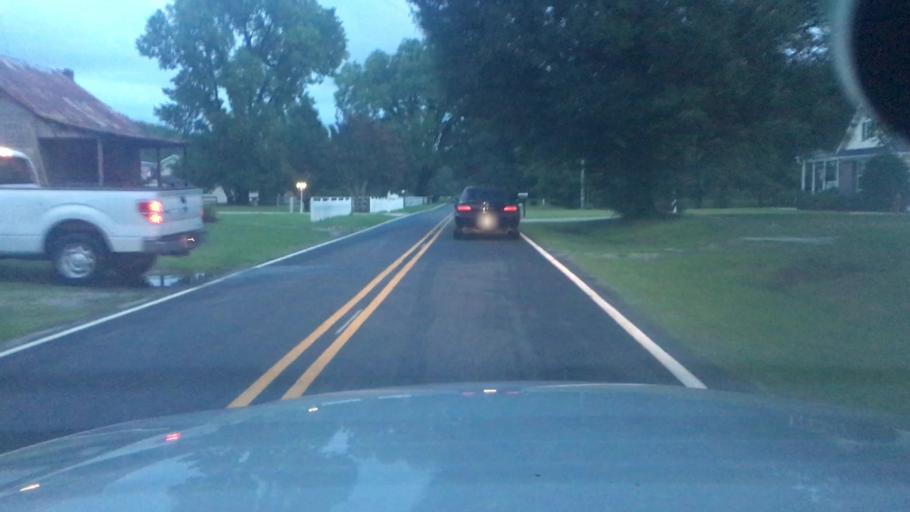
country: US
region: North Carolina
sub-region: Cumberland County
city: Hope Mills
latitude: 34.9656
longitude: -78.9275
